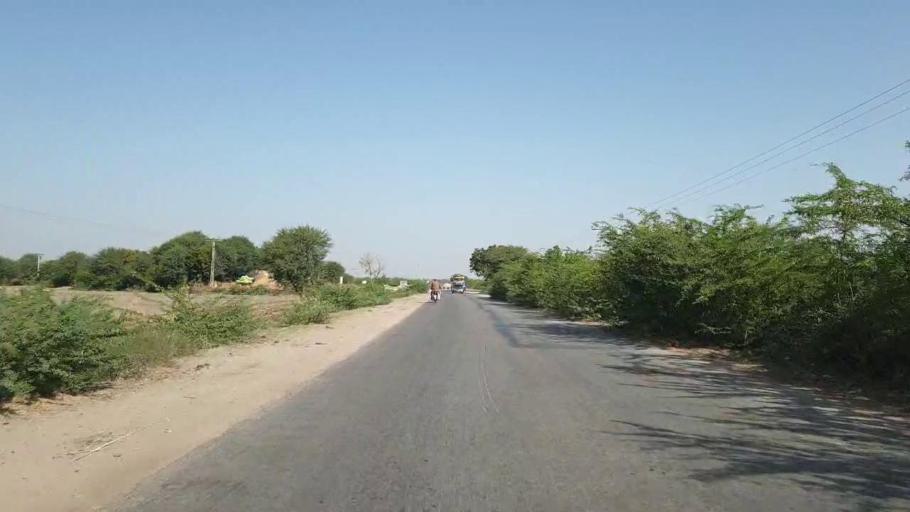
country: PK
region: Sindh
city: Chor
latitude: 25.4884
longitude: 69.7816
